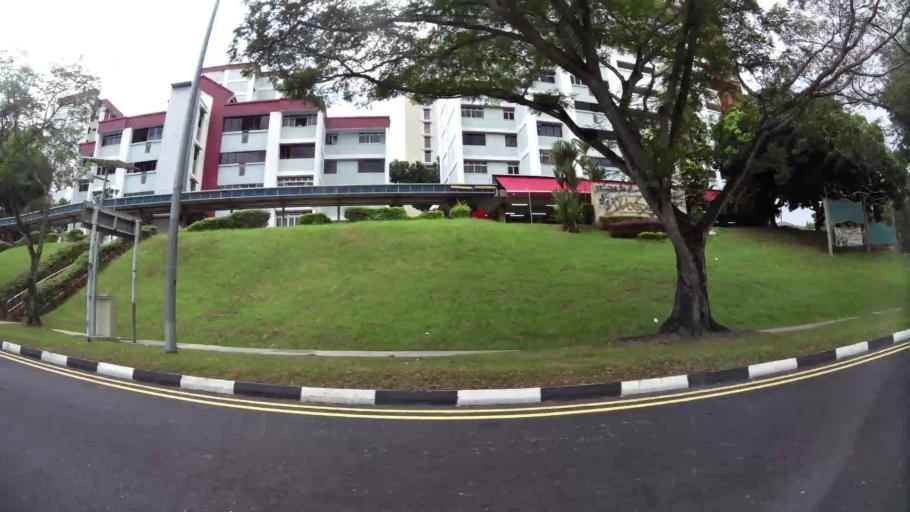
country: MY
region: Johor
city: Johor Bahru
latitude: 1.4375
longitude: 103.7826
